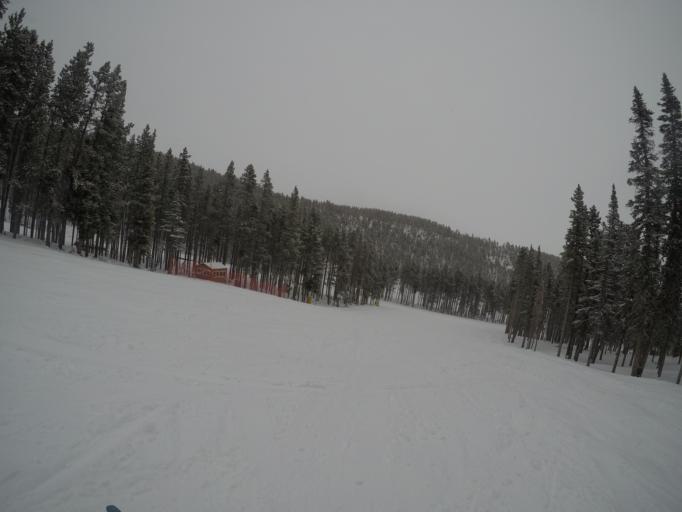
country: US
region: Montana
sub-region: Carbon County
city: Red Lodge
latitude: 45.1908
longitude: -109.3470
